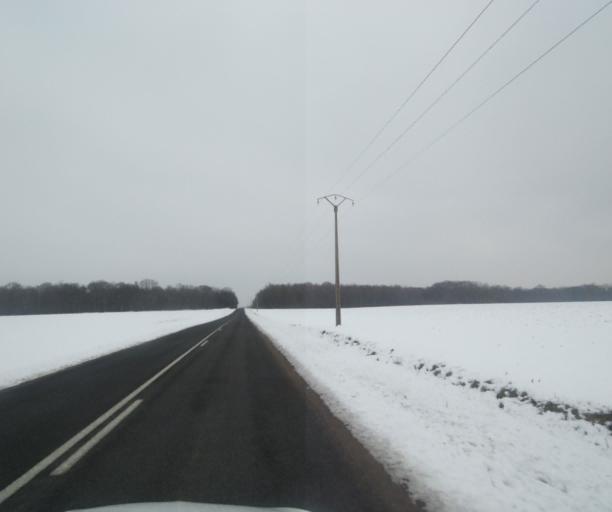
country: FR
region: Champagne-Ardenne
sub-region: Departement de la Haute-Marne
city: Villiers-en-Lieu
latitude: 48.6066
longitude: 4.8818
